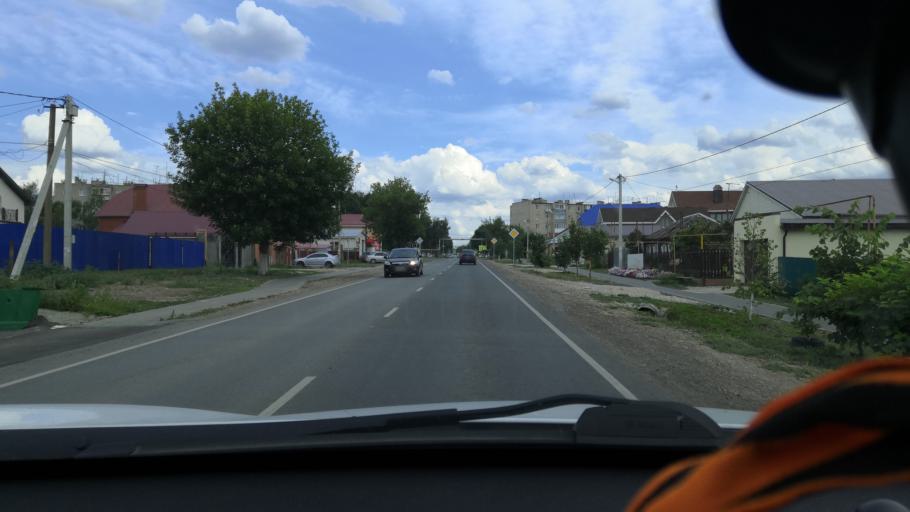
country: RU
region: Samara
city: Novosemeykino
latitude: 53.3730
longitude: 50.3499
